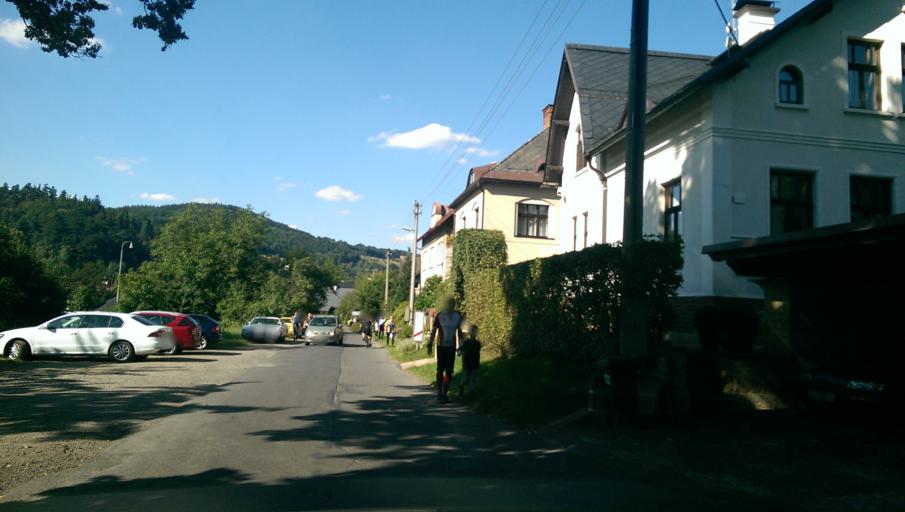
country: CZ
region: Liberecky
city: Mala Skala
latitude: 50.6359
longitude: 15.1931
